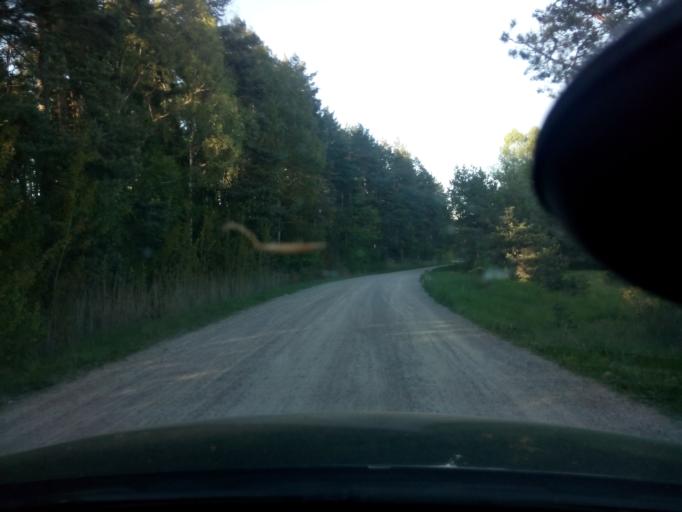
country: SE
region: Soedermanland
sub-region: Nykopings Kommun
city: Nykoping
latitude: 58.7780
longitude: 17.0442
